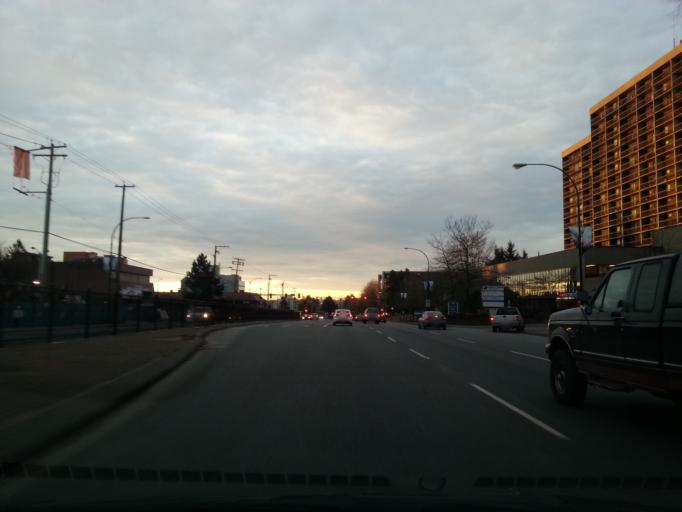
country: CA
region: British Columbia
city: New Westminster
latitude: 49.1820
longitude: -122.8456
